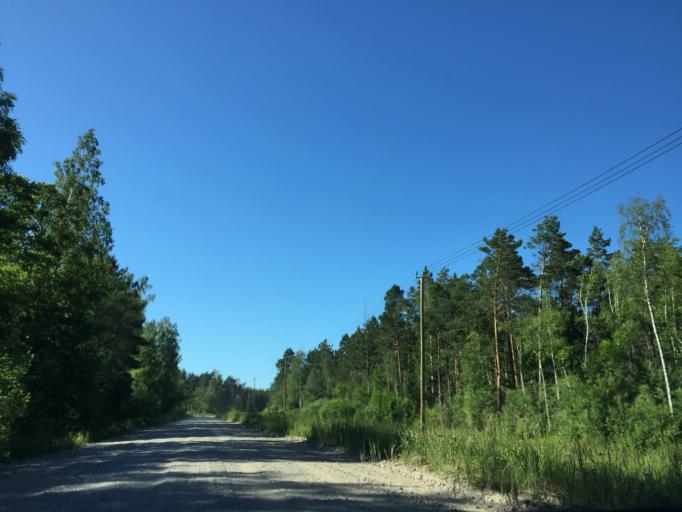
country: LV
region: Ventspils
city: Ventspils
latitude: 57.5608
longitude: 21.7289
